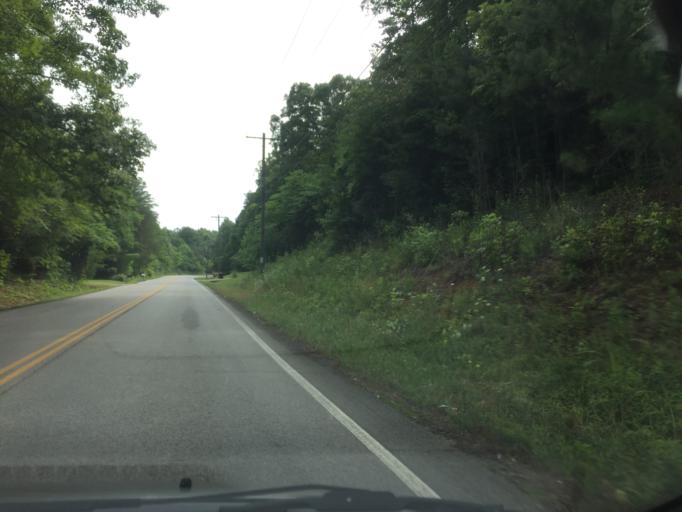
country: US
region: Tennessee
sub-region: Hamilton County
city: Apison
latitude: 35.0099
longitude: -85.0443
